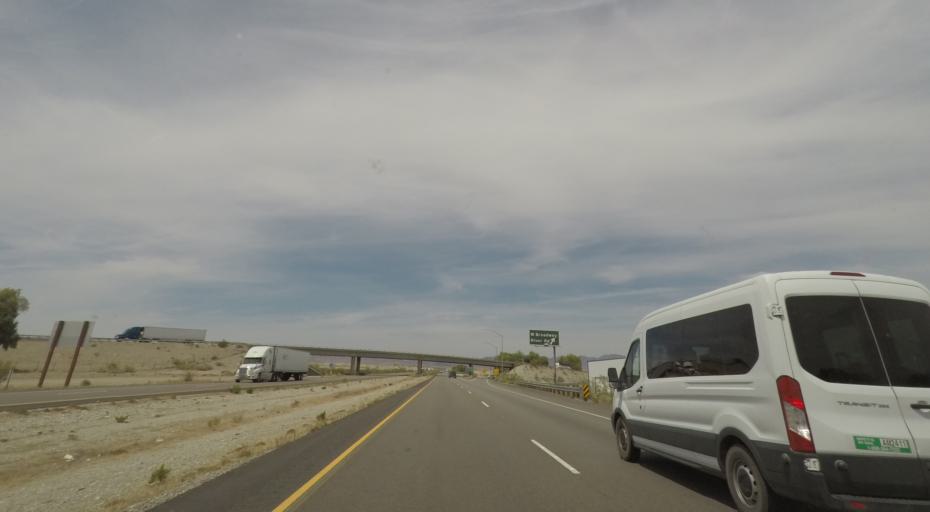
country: US
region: California
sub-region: San Bernardino County
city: Needles
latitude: 34.8529
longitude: -114.6248
